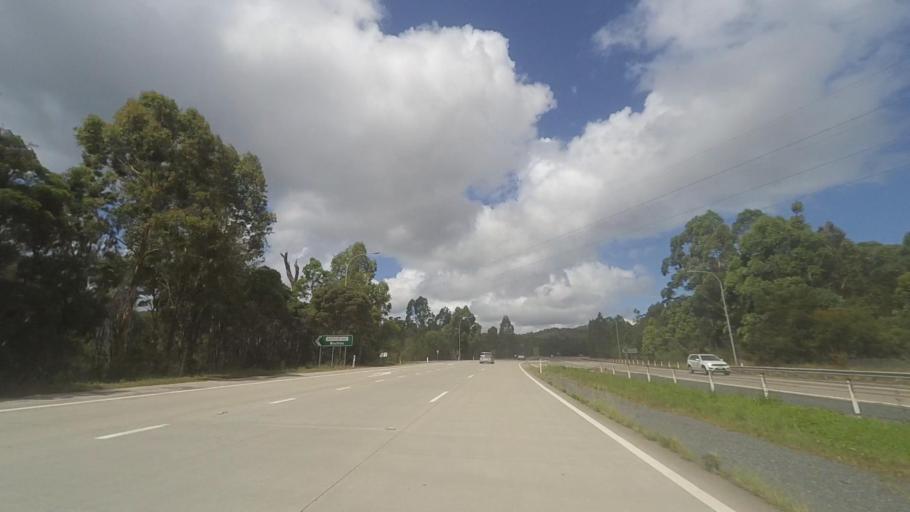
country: AU
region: New South Wales
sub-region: Great Lakes
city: Bulahdelah
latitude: -32.3865
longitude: 152.2290
